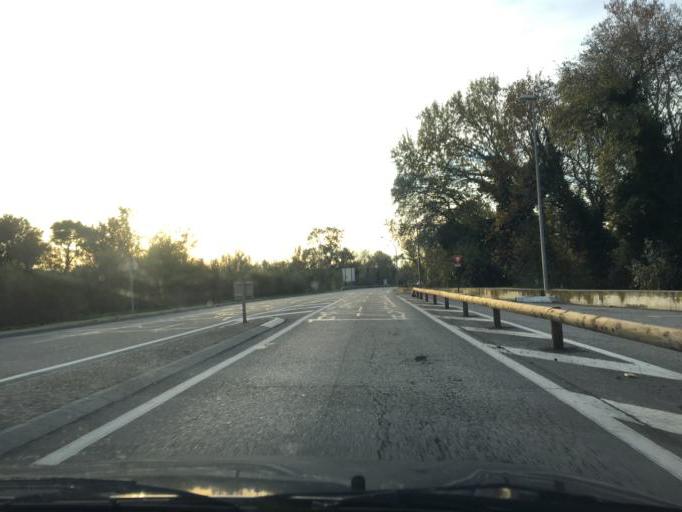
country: FR
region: Provence-Alpes-Cote d'Azur
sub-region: Departement du Vaucluse
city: Cavaillon
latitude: 43.8270
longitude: 5.0348
